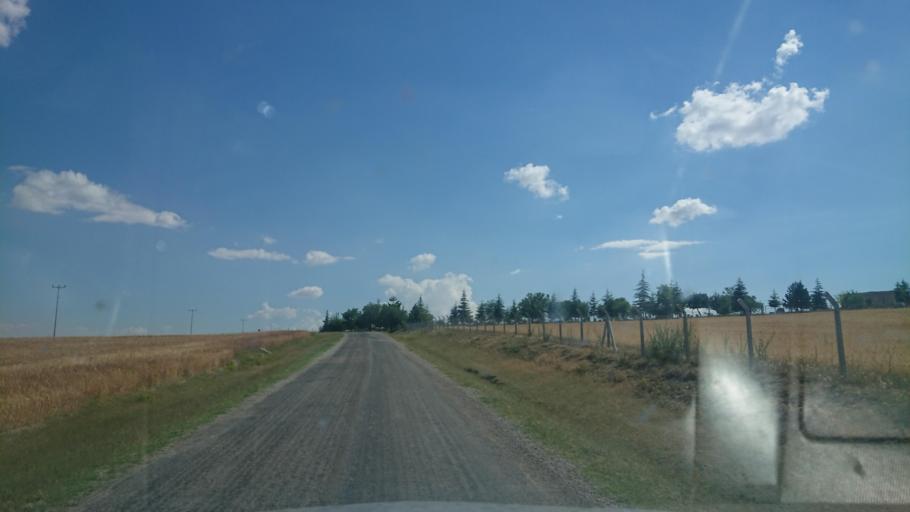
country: TR
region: Aksaray
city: Agacoren
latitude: 38.7644
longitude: 33.7831
